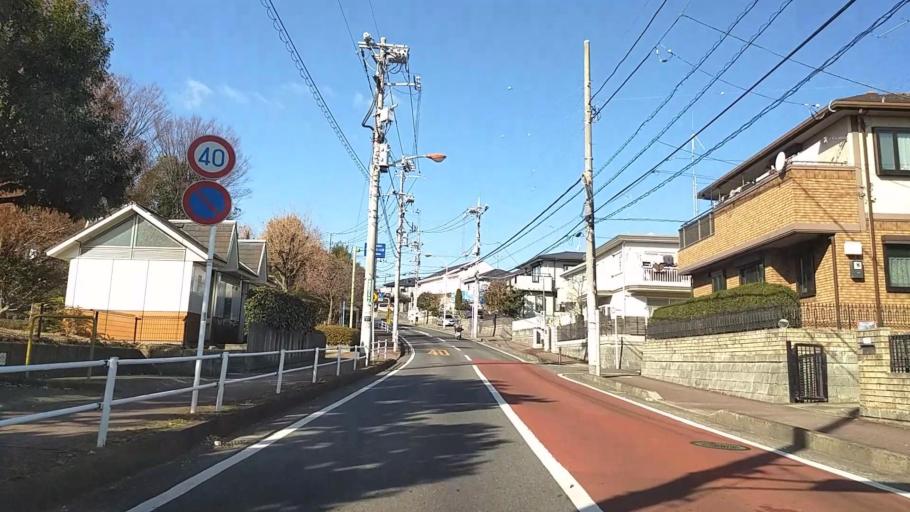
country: JP
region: Kanagawa
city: Isehara
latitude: 35.3944
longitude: 139.3089
